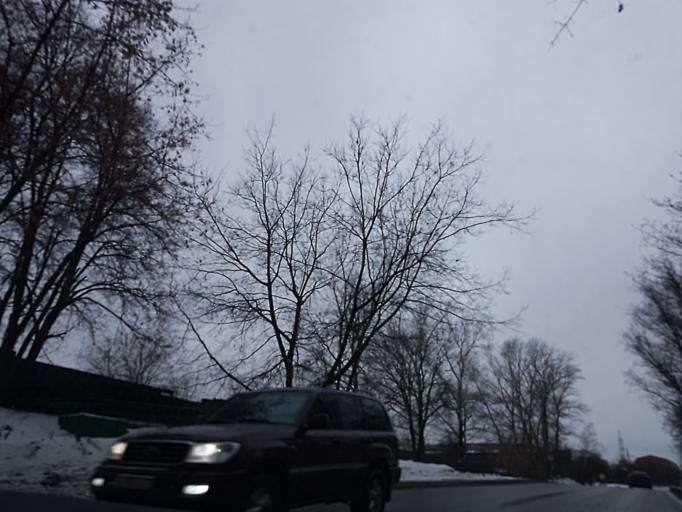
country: RU
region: Moskovskaya
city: Pavshino
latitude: 55.8215
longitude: 37.3576
